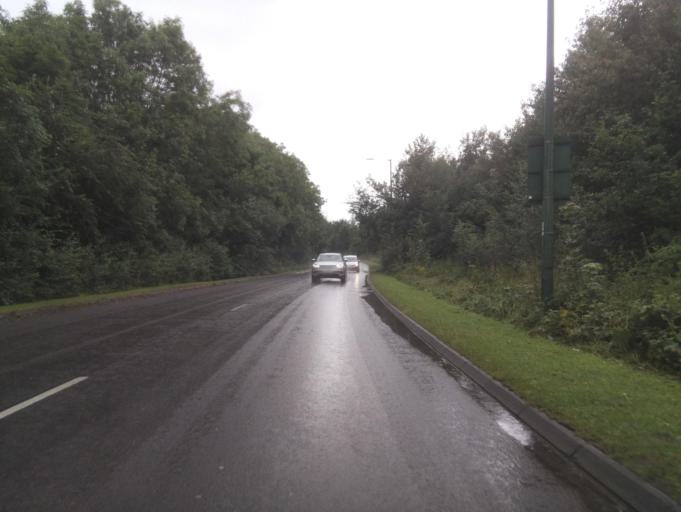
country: GB
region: England
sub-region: Solihull
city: Solihull
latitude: 52.4089
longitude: -1.7549
